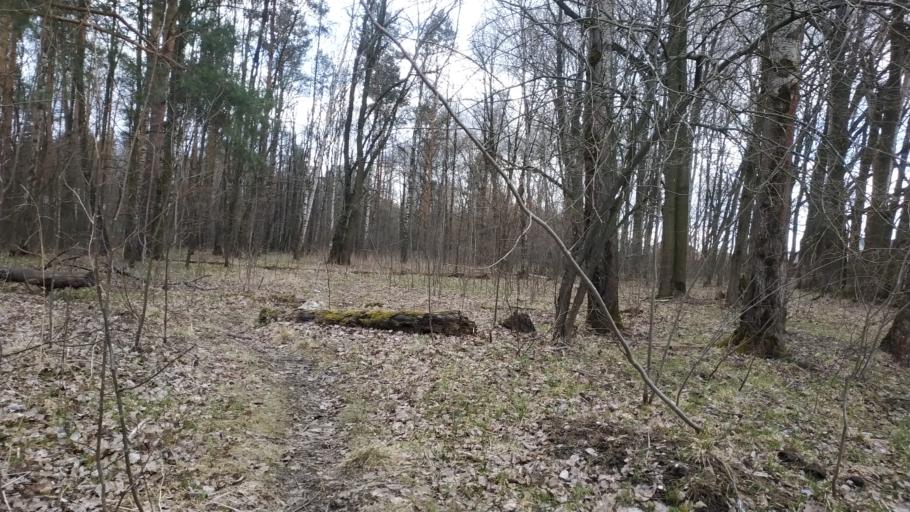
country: RU
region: Moskovskaya
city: Malyshevo
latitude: 55.5502
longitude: 38.3202
